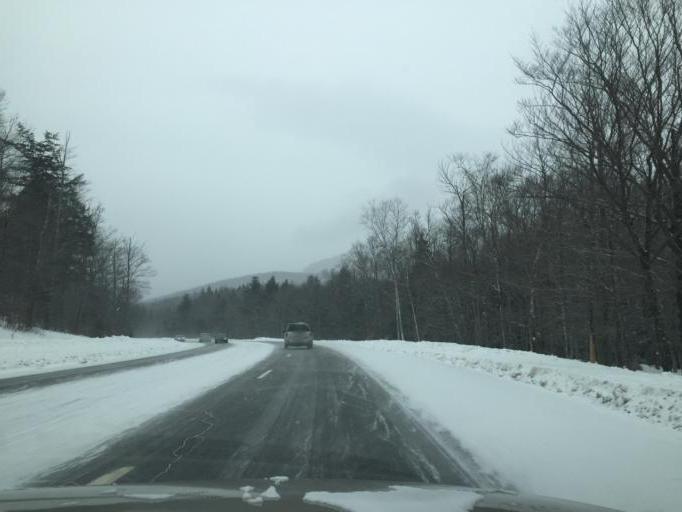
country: US
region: New Hampshire
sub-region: Coos County
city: Gorham
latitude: 44.2088
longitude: -71.2415
